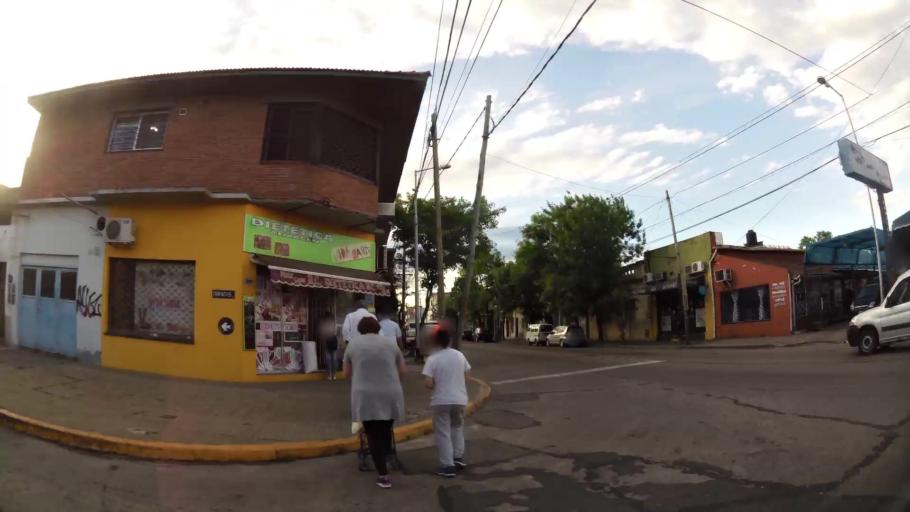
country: AR
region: Buenos Aires
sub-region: Partido de Avellaneda
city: Avellaneda
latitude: -34.6896
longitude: -58.3408
